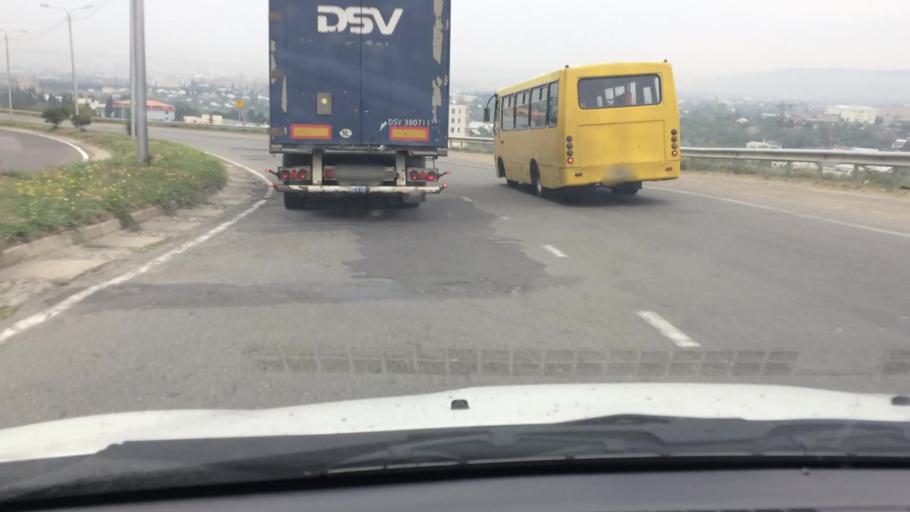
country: GE
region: T'bilisi
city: Tbilisi
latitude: 41.6512
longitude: 44.9050
